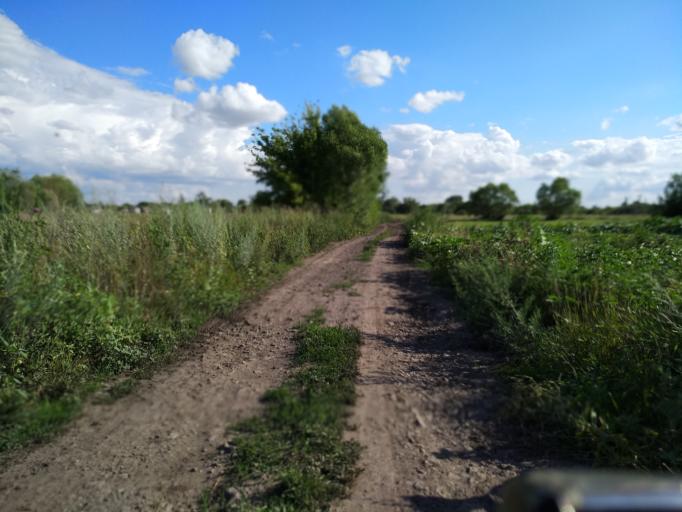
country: RU
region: Lipetsk
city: Dobrinka
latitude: 52.0285
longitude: 40.5622
